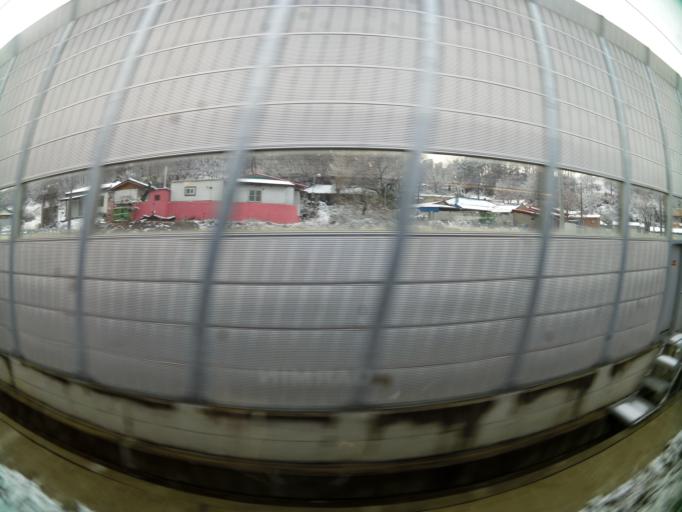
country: KR
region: Daejeon
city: Daejeon
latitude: 36.3174
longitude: 127.4518
